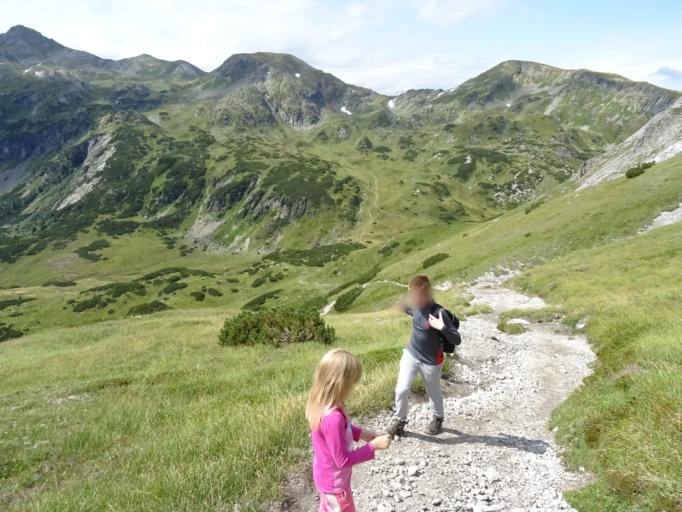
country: AT
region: Salzburg
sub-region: Politischer Bezirk Tamsweg
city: Tweng
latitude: 47.2795
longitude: 13.6096
